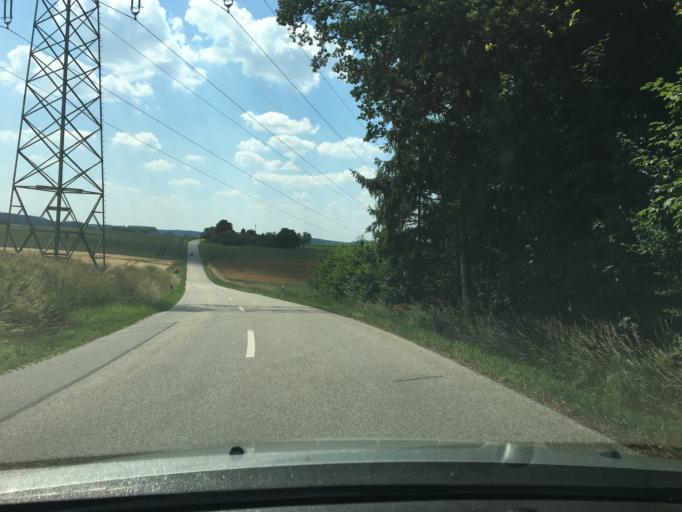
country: DE
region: Bavaria
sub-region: Upper Bavaria
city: Egglkofen
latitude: 48.4244
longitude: 12.4390
